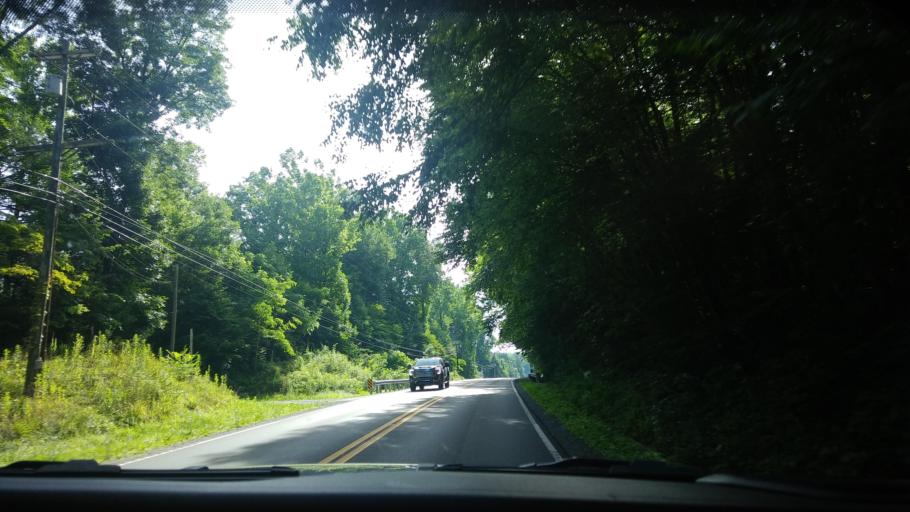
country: US
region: Tennessee
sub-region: Sevier County
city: Gatlinburg
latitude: 35.7611
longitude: -83.3342
